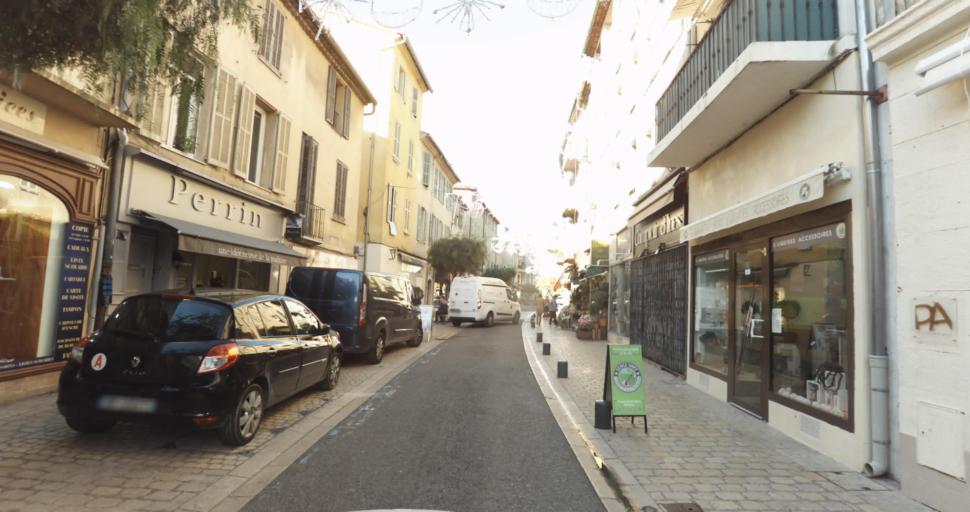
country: FR
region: Provence-Alpes-Cote d'Azur
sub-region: Departement des Alpes-Maritimes
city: Vence
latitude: 43.7219
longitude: 7.1136
